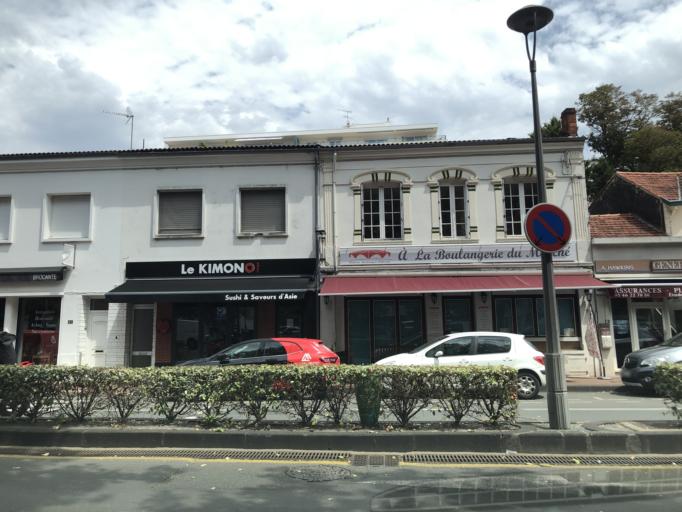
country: FR
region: Poitou-Charentes
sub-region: Departement de la Charente-Maritime
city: Royan
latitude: 45.6283
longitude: -1.0316
